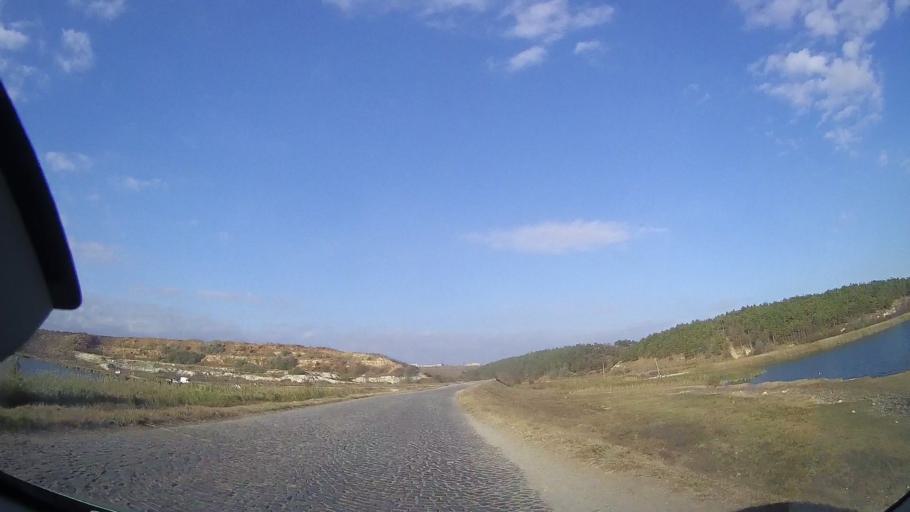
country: RO
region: Constanta
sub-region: Comuna Limanu
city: Limanu
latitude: 43.8127
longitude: 28.5169
